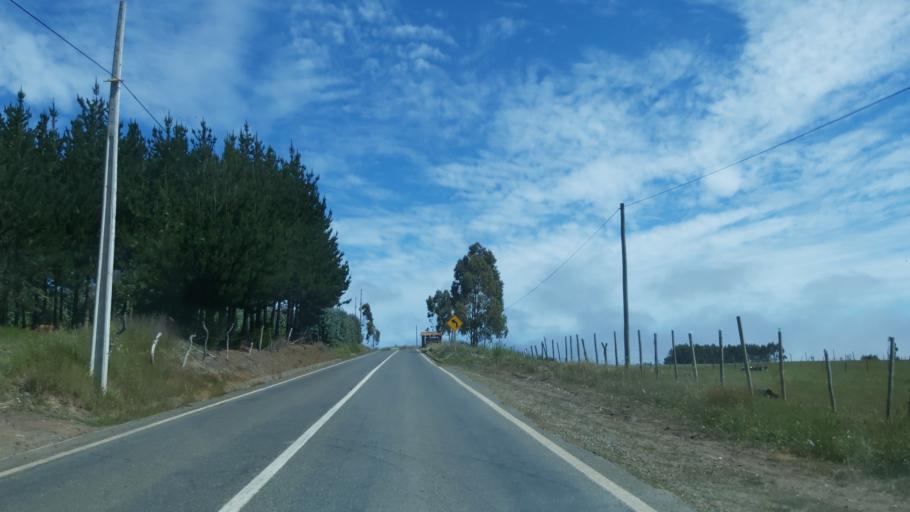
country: CL
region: Maule
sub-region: Provincia de Talca
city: Constitucion
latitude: -35.5742
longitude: -72.6028
